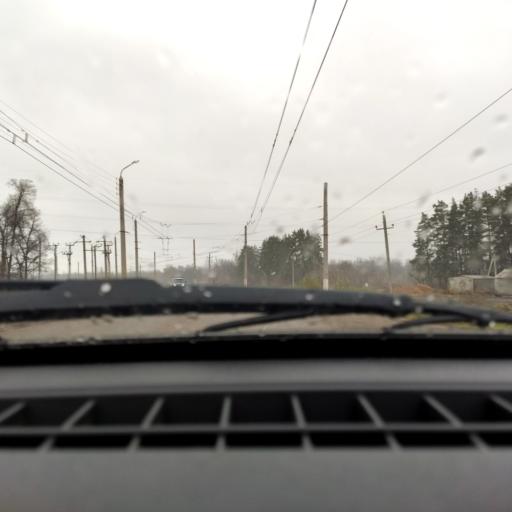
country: RU
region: Bashkortostan
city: Ufa
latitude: 54.7829
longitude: 55.9479
